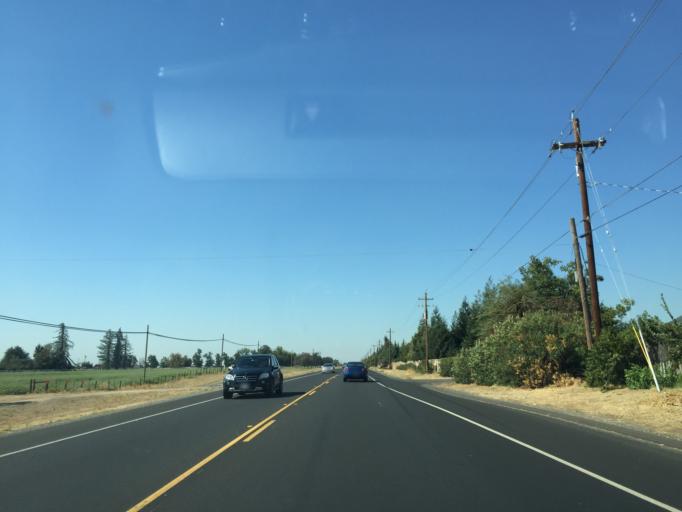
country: US
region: California
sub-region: Stanislaus County
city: East Oakdale
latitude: 37.7765
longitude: -120.7842
